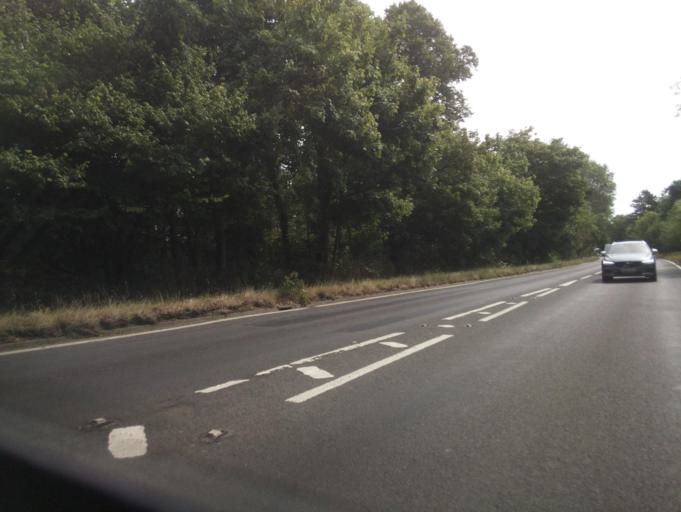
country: GB
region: England
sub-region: Surrey
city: Headley
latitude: 51.2449
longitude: -0.2577
